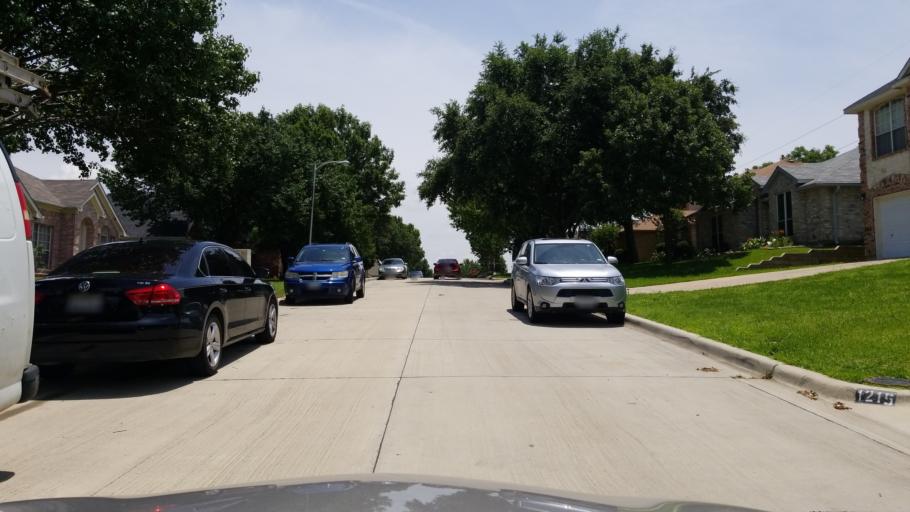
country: US
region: Texas
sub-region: Dallas County
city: Grand Prairie
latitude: 32.6815
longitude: -96.9902
